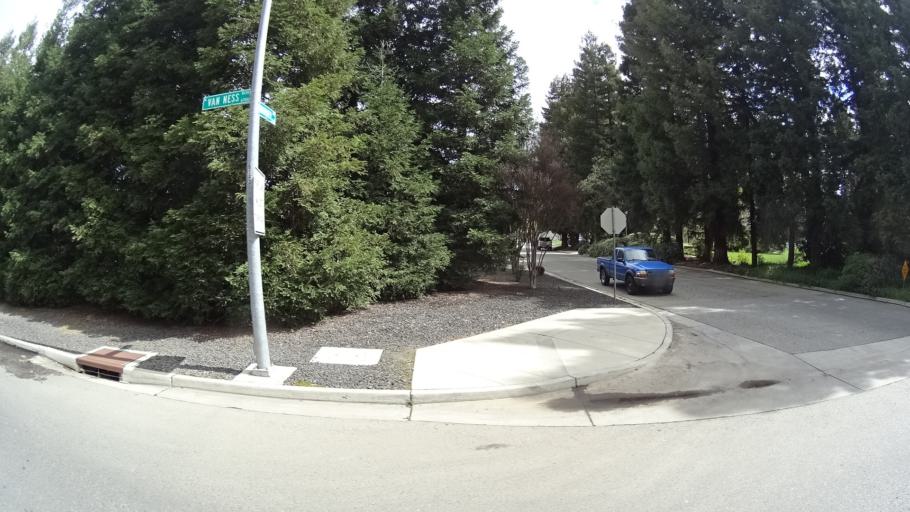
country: US
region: California
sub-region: Fresno County
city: Fresno
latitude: 36.8364
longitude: -119.8353
